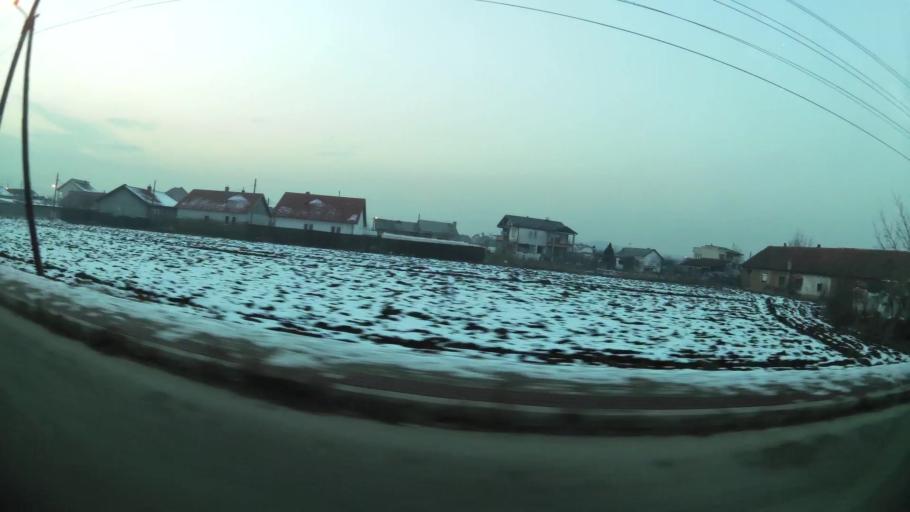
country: MK
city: Creshevo
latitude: 42.0043
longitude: 21.5168
